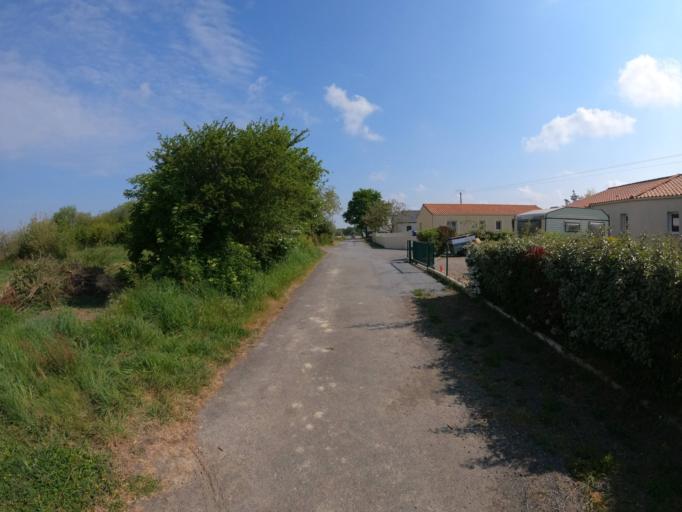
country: FR
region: Pays de la Loire
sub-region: Departement de la Vendee
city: Montaigu
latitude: 47.0033
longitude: -1.2880
